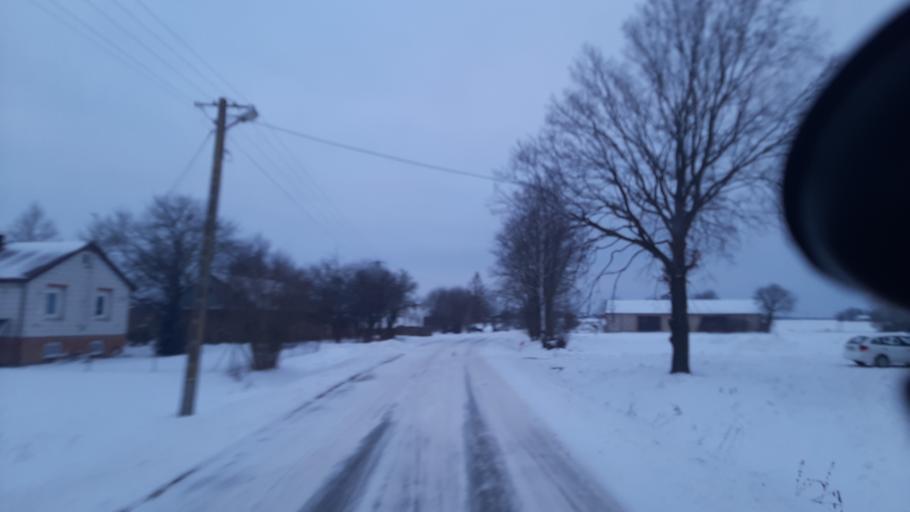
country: PL
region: Lublin Voivodeship
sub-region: Powiat lubelski
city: Jastkow
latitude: 51.3449
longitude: 22.4103
